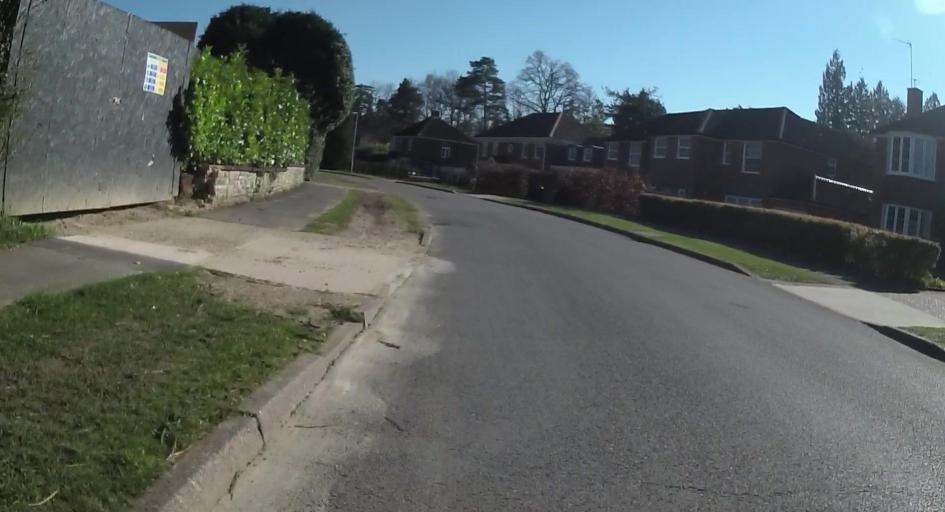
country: GB
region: England
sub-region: Royal Borough of Windsor and Maidenhead
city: Ascot
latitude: 51.3997
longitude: -0.6651
